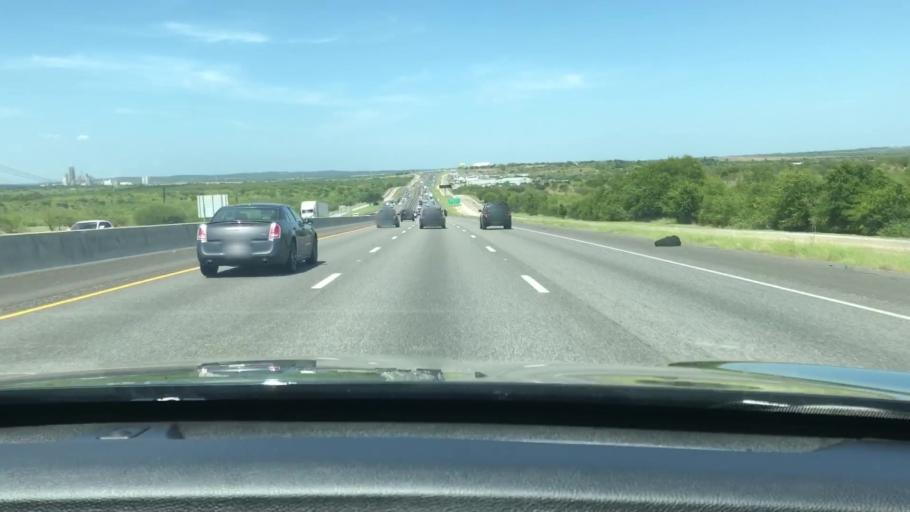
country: US
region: Texas
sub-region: Guadalupe County
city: Lake Dunlap
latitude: 29.7584
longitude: -98.0485
